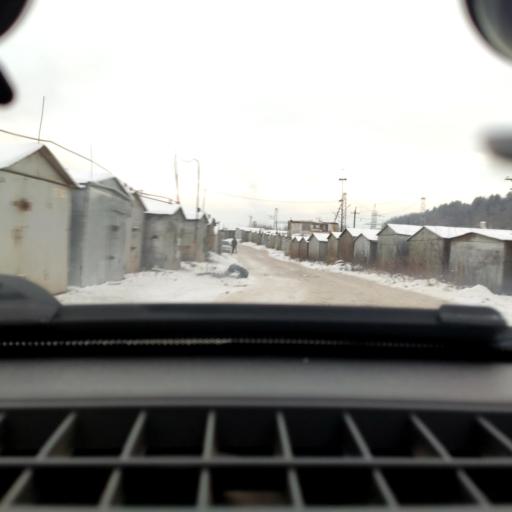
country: RU
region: Bashkortostan
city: Ufa
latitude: 54.8065
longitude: 56.1406
